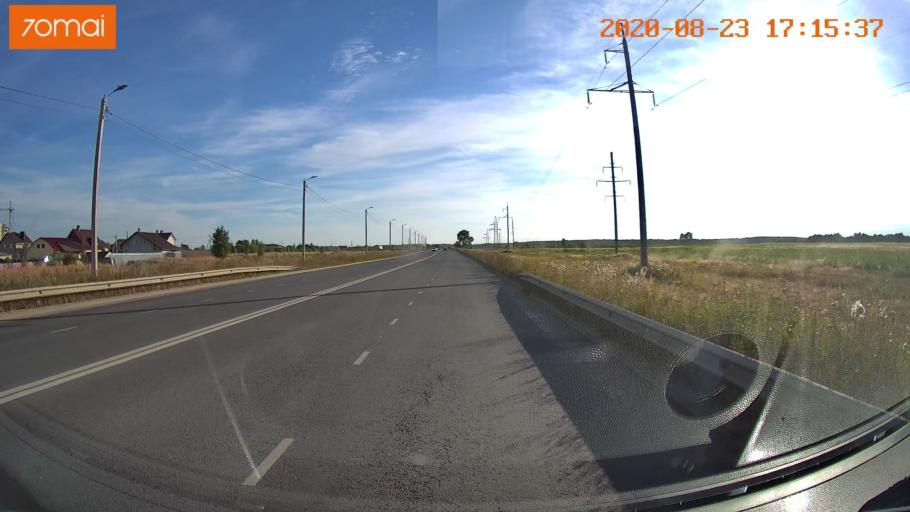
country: RU
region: Ivanovo
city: Novo-Talitsy
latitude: 57.0442
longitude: 40.9106
